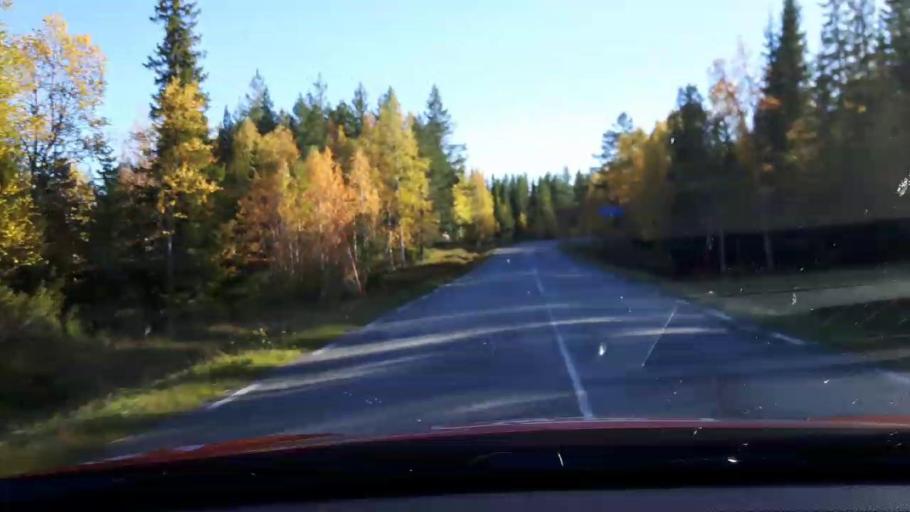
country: SE
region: Jaemtland
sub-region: OEstersunds Kommun
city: Lit
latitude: 63.8325
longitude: 14.8748
